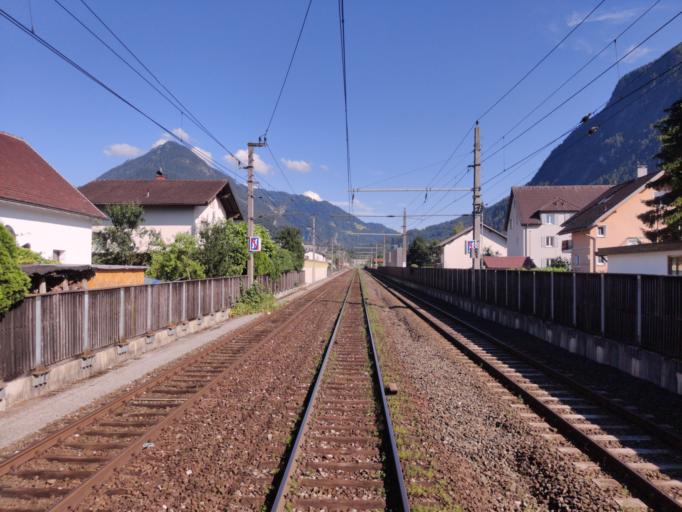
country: AT
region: Vorarlberg
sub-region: Politischer Bezirk Bludenz
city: Bludenz
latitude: 47.1490
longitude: 9.8229
